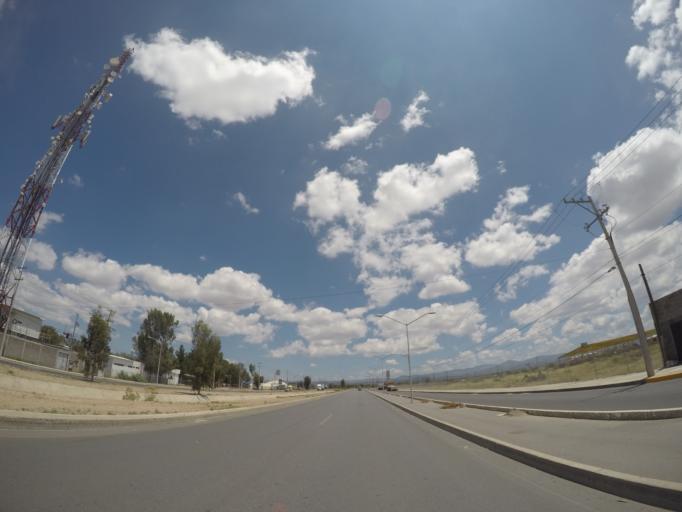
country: MX
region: San Luis Potosi
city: La Pila
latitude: 22.0512
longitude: -100.8649
